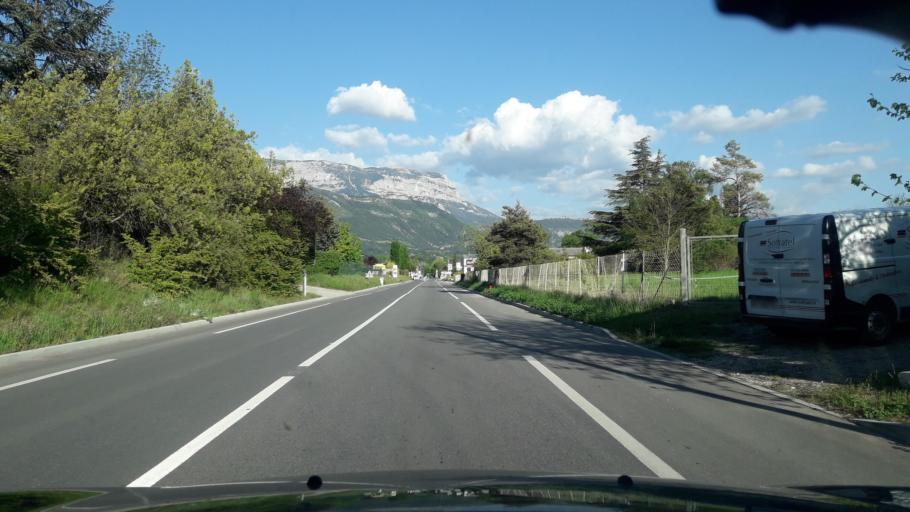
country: FR
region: Rhone-Alpes
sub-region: Departement de la Drome
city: Die
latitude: 44.7624
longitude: 5.3499
